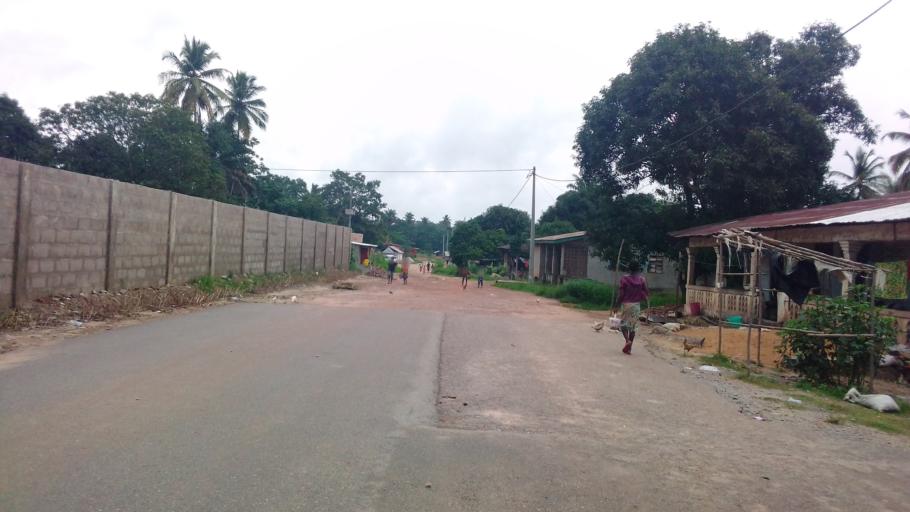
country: SL
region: Northern Province
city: Lunsar
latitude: 8.6841
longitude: -12.5376
